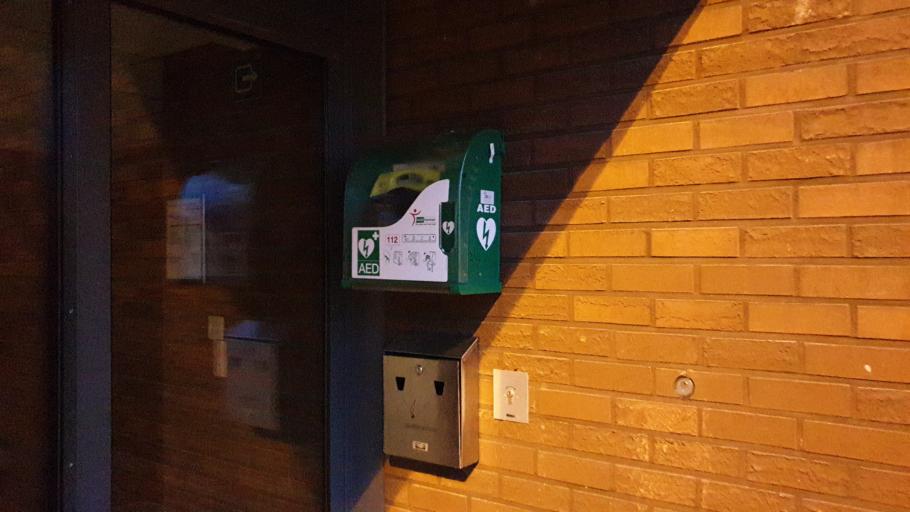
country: BE
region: Flanders
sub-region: Provincie Oost-Vlaanderen
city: Sint-Gillis-Waas
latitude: 51.2177
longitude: 4.1243
